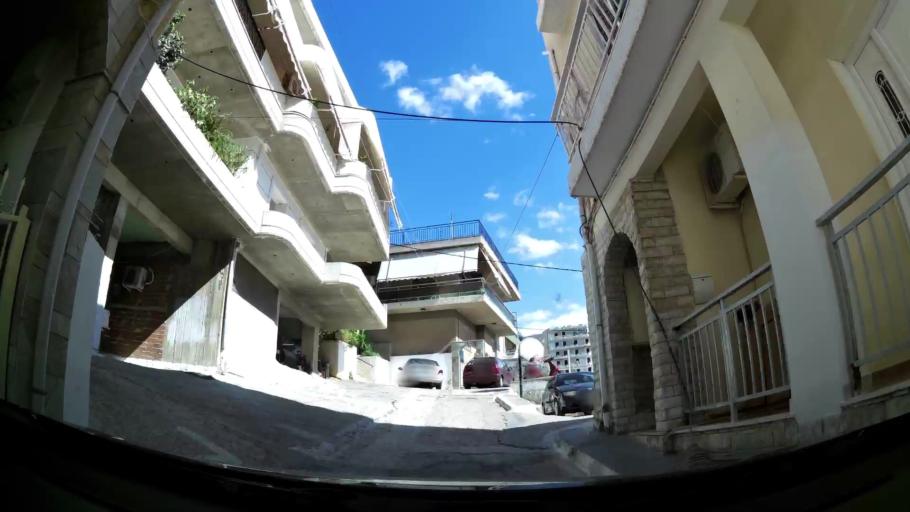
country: GR
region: Attica
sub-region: Nomos Piraios
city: Perama
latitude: 37.9685
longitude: 23.5723
